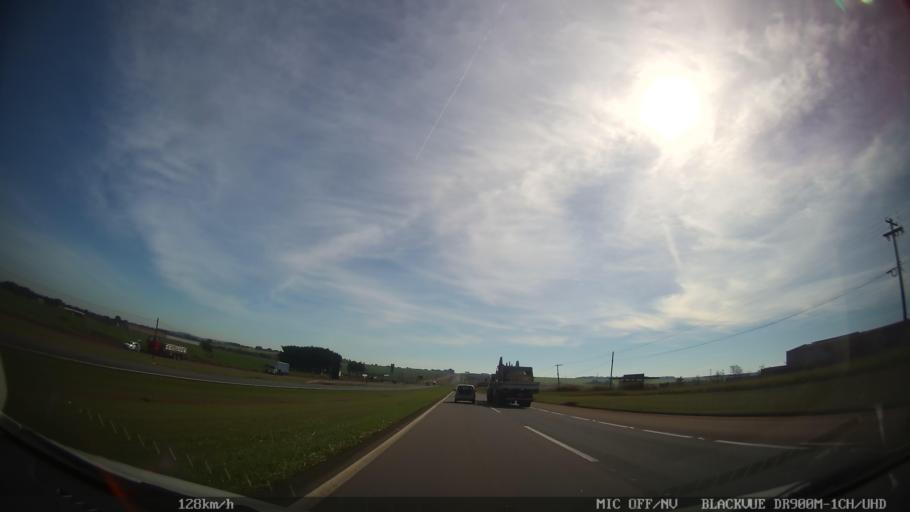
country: BR
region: Sao Paulo
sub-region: Cordeiropolis
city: Cordeiropolis
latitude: -22.4896
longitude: -47.3992
